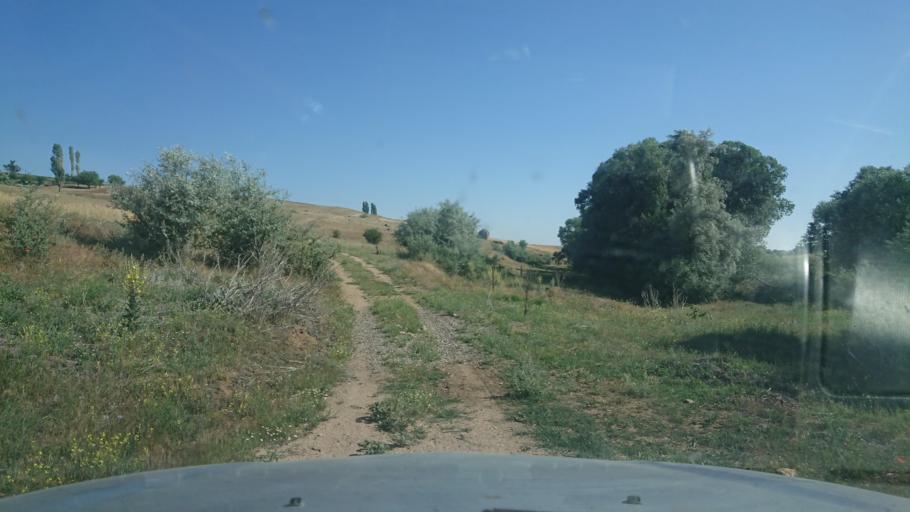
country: TR
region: Aksaray
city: Agacoren
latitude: 38.8446
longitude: 33.9268
